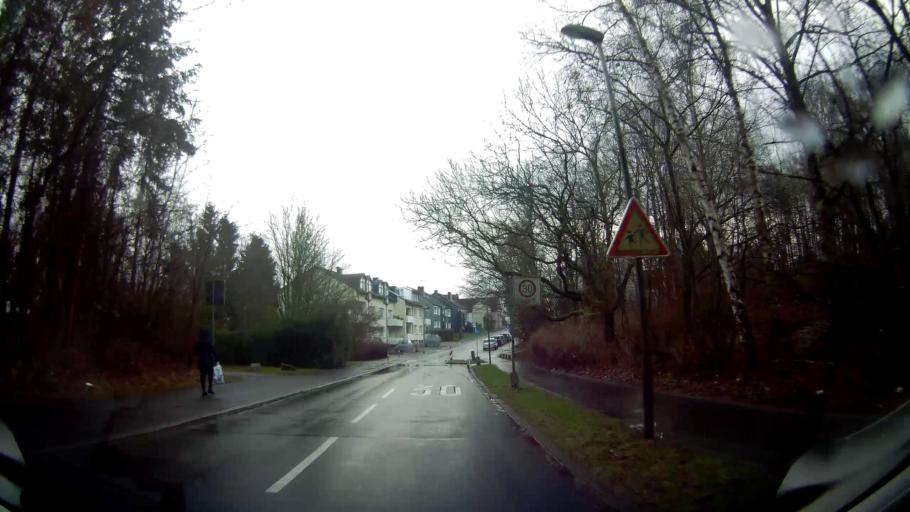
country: DE
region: North Rhine-Westphalia
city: Castrop-Rauxel
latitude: 51.5048
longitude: 7.2836
